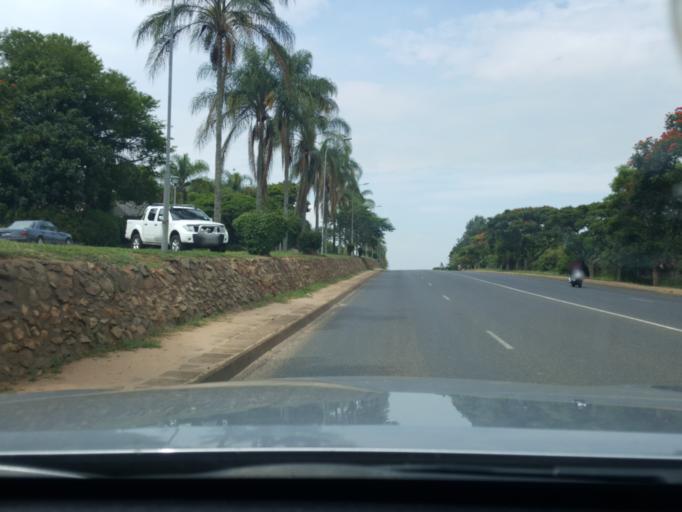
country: ZA
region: Mpumalanga
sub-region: Ehlanzeni District
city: White River
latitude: -25.3341
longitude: 31.0051
